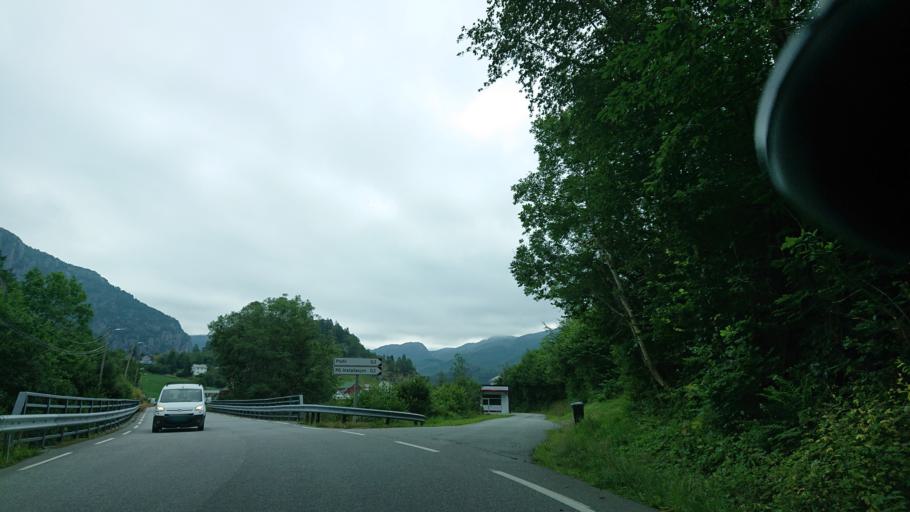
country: NO
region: Rogaland
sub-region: Hjelmeland
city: Hjelmelandsvagen
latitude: 59.2350
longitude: 6.1836
